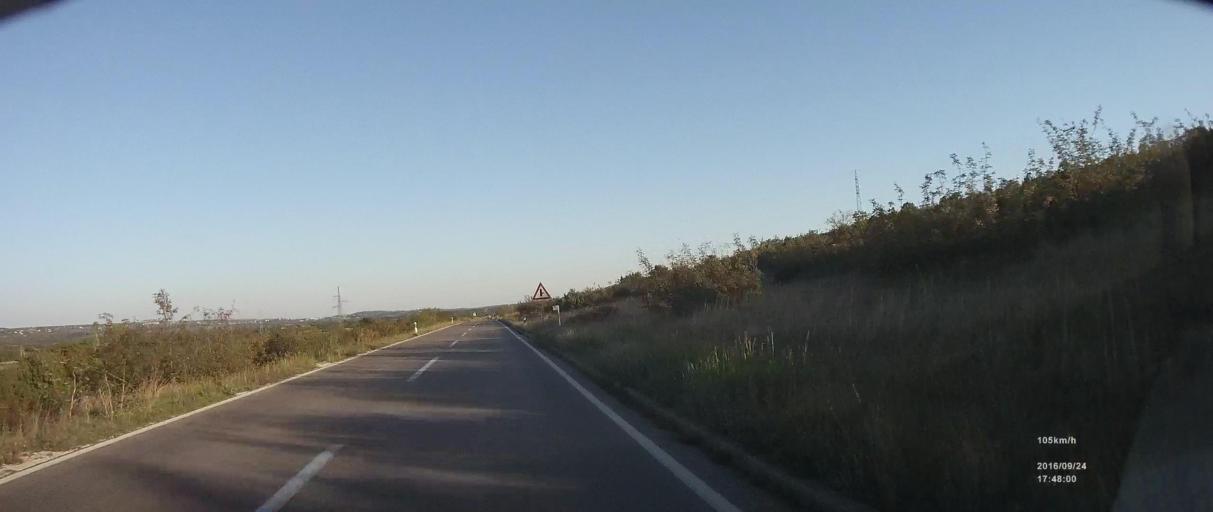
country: HR
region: Zadarska
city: Polaca
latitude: 44.0685
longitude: 15.5316
